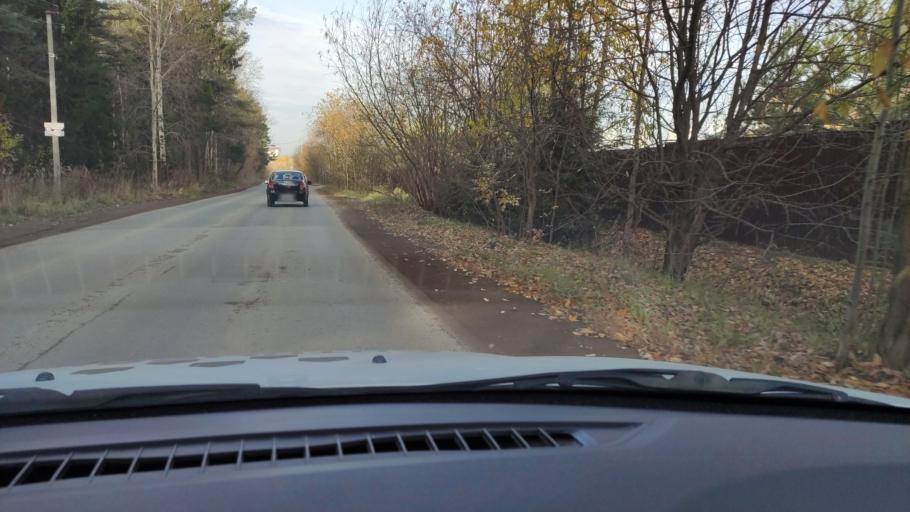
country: RU
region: Perm
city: Perm
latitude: 57.9966
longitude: 56.3326
